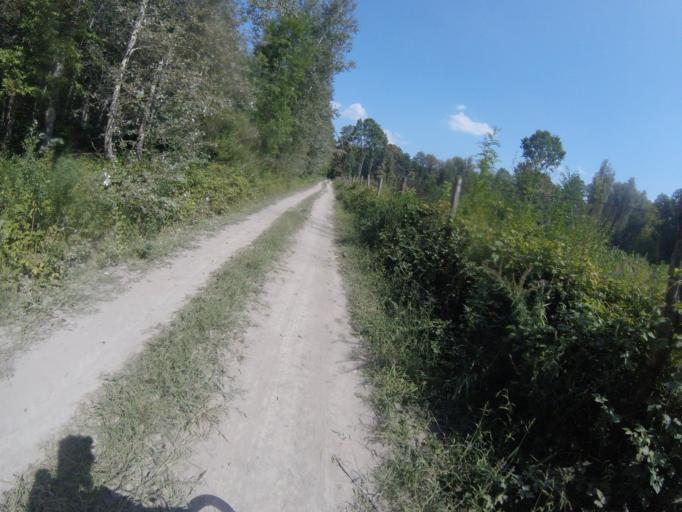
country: HU
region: Tolna
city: Bata
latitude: 46.2006
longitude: 18.8437
